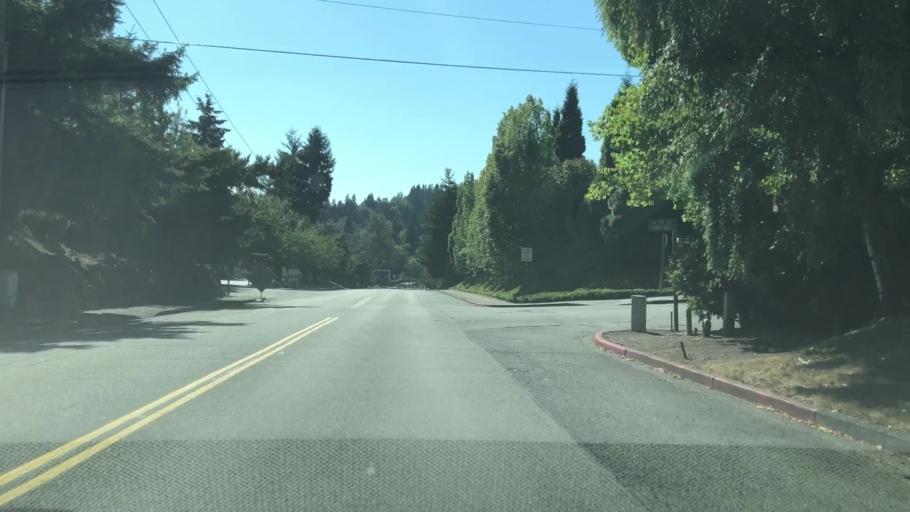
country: US
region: Washington
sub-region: King County
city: Woodinville
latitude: 47.7725
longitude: -122.1502
